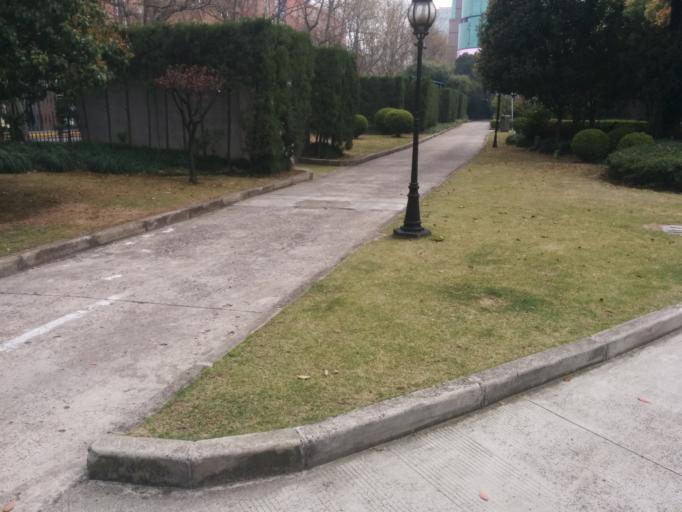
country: CN
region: Shanghai Shi
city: Shanghai
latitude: 31.2213
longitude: 121.4559
